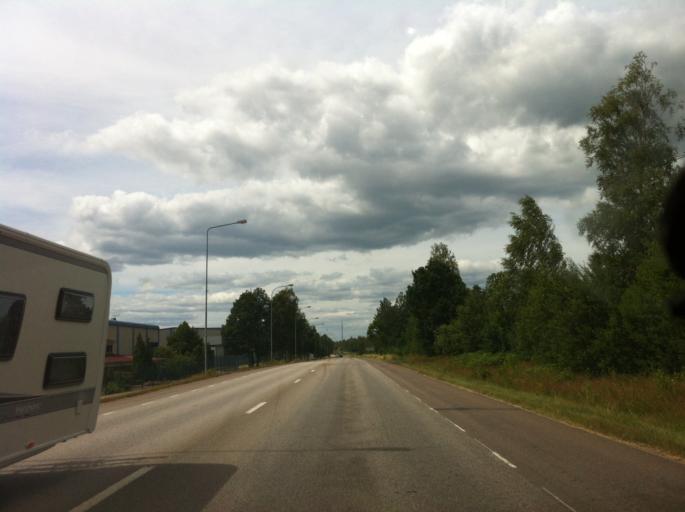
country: SE
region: Kalmar
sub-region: Emmaboda Kommun
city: Emmaboda
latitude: 56.6251
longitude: 15.5653
